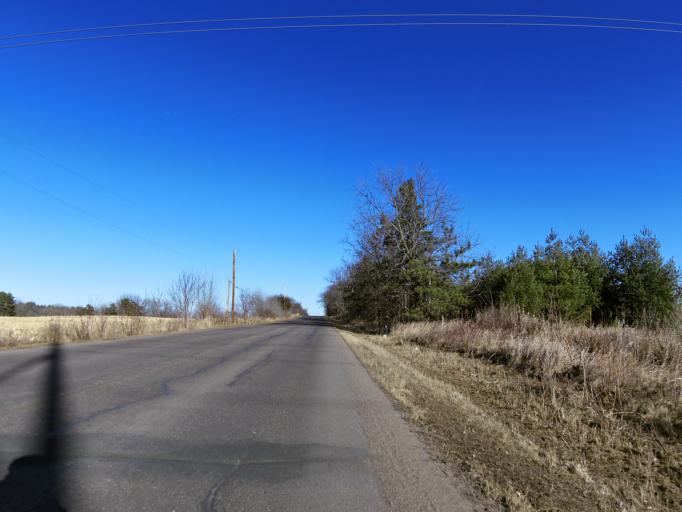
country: US
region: Minnesota
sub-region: Washington County
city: Oak Park Heights
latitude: 44.9925
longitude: -92.8169
